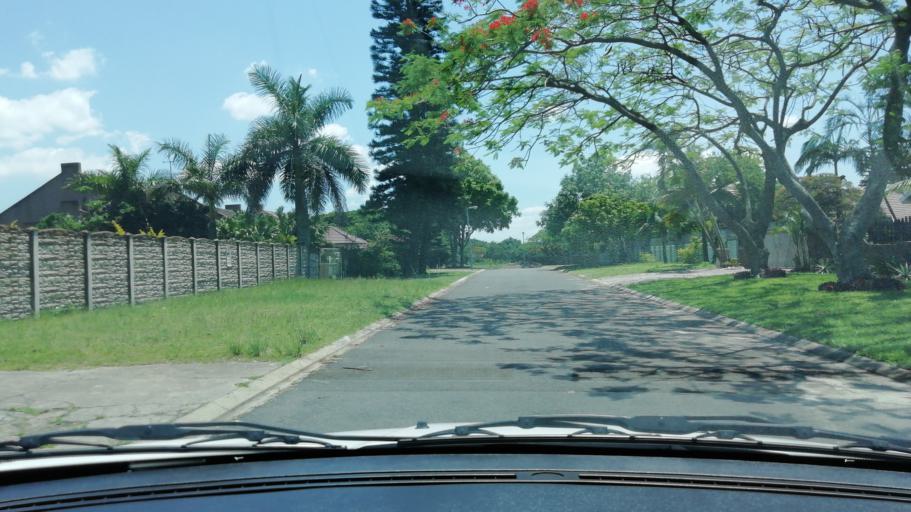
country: ZA
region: KwaZulu-Natal
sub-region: uThungulu District Municipality
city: Richards Bay
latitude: -28.7366
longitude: 32.0461
